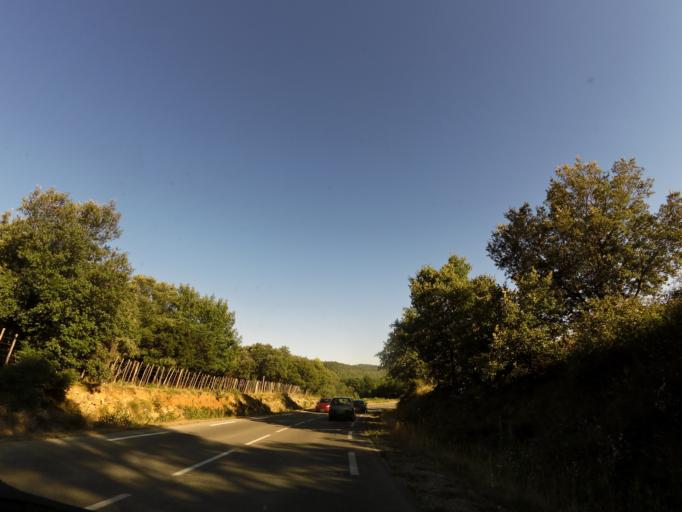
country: FR
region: Languedoc-Roussillon
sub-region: Departement du Gard
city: Quissac
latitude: 43.8724
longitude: 4.0152
